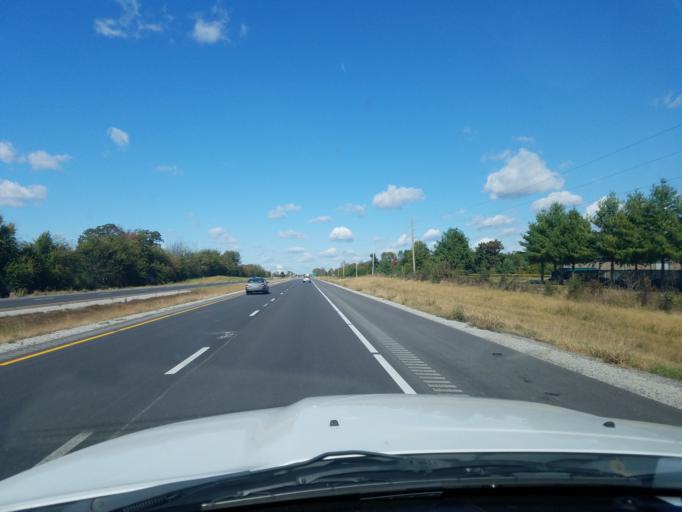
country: US
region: Kentucky
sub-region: Warren County
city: Plano
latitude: 36.9178
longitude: -86.4438
